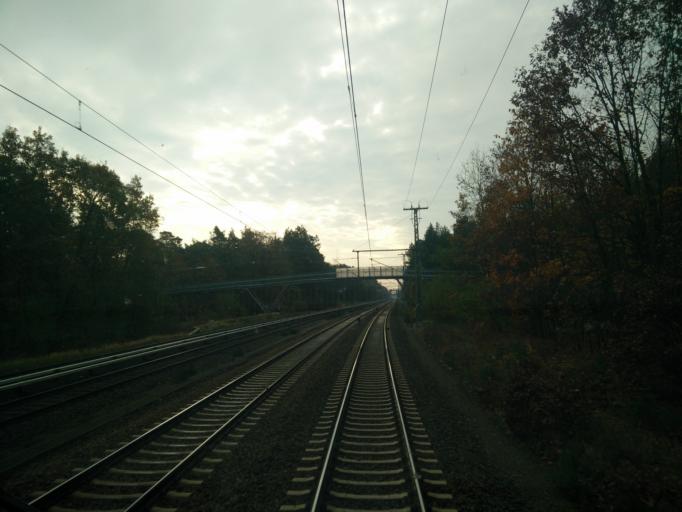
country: DE
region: Berlin
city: Bohnsdorf
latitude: 52.3933
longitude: 13.6009
